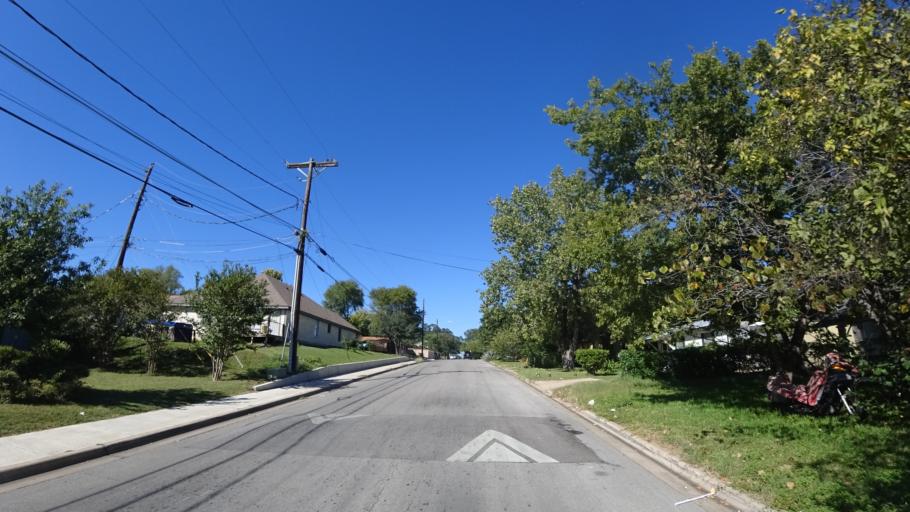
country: US
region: Texas
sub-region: Travis County
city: Austin
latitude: 30.2835
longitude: -97.7019
